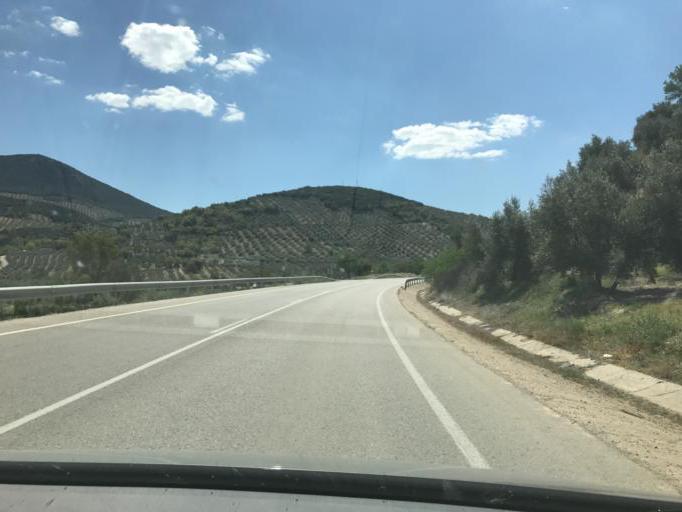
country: ES
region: Andalusia
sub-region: Provincia de Granada
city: Benalua de las Villas
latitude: 37.4411
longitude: -3.6525
